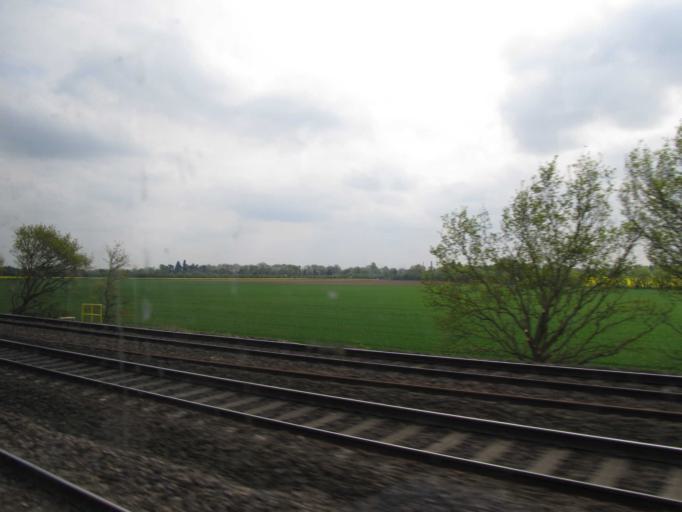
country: GB
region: England
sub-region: Surrey
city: Colnbrook
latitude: 51.5077
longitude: -0.5257
